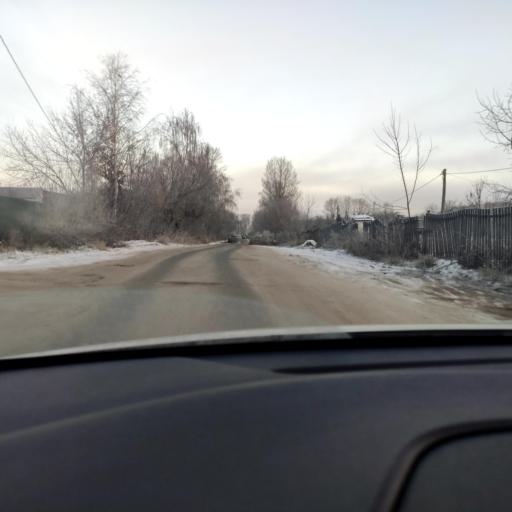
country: RU
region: Tatarstan
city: Staroye Arakchino
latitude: 55.8637
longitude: 49.0468
